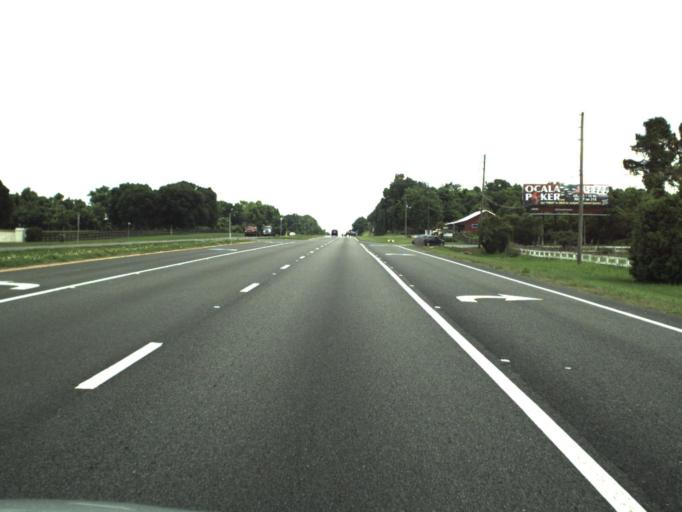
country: US
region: Florida
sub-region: Marion County
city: Ocala
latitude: 29.2875
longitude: -82.1518
